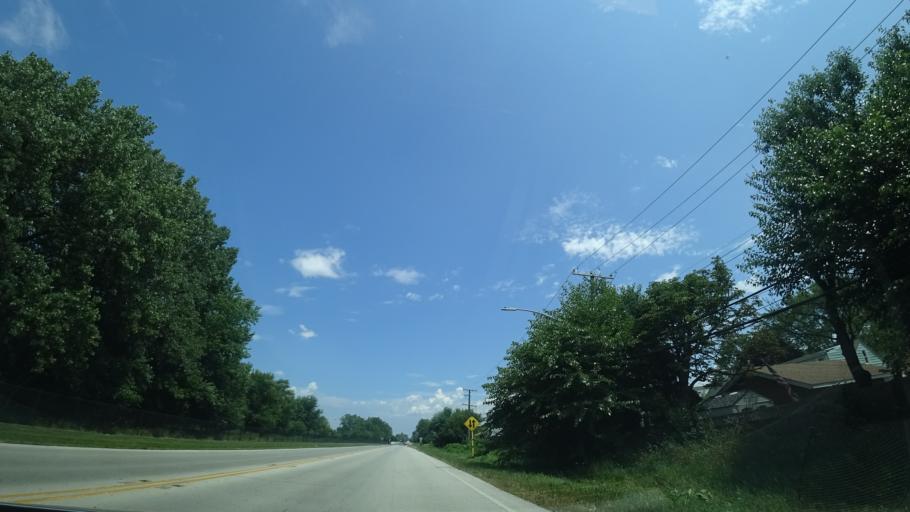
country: US
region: Illinois
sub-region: Cook County
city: Alsip
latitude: 41.6837
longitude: -87.7346
